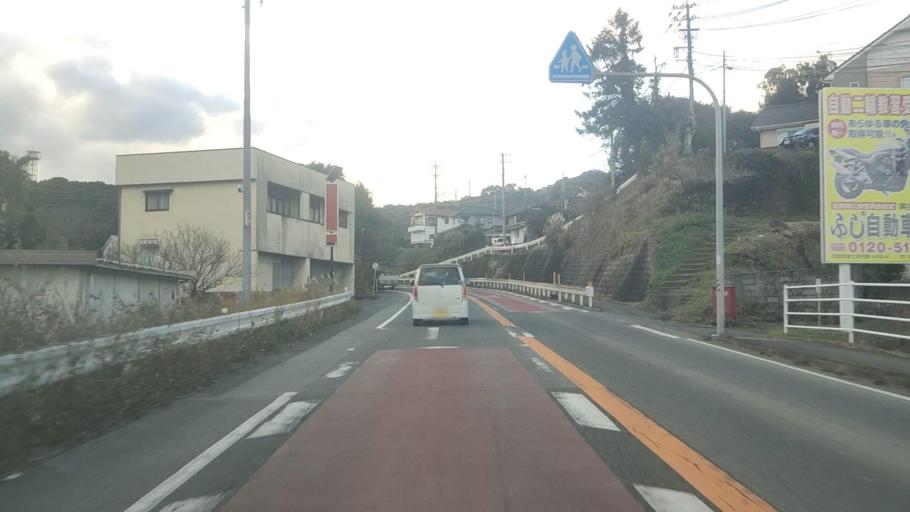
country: JP
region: Saga Prefecture
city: Saga-shi
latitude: 33.2906
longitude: 130.1701
